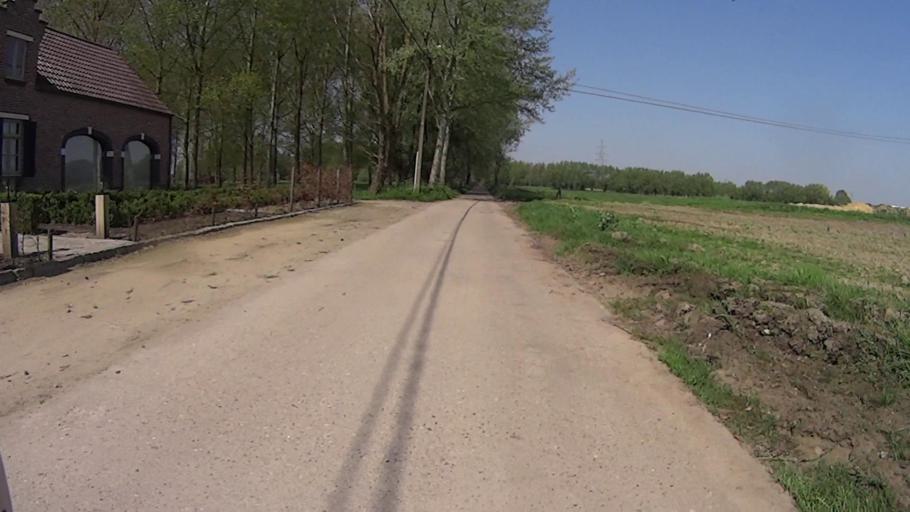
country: BE
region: Flanders
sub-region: Provincie Antwerpen
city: Sint-Amands
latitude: 51.0532
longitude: 4.2272
